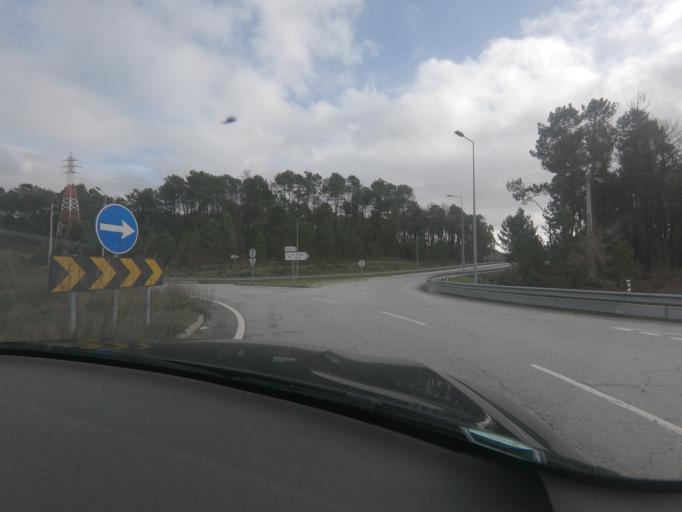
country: PT
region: Viseu
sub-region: Viseu
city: Campo
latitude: 40.7066
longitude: -7.9446
